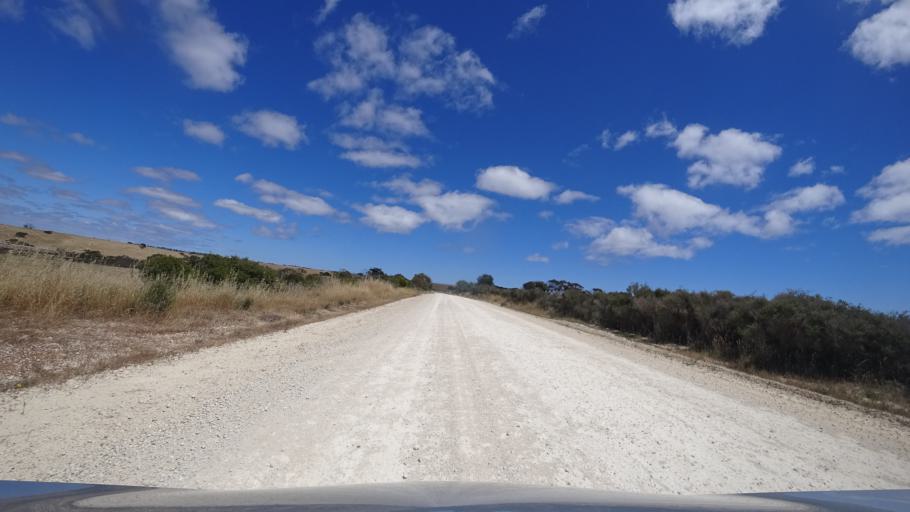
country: AU
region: South Australia
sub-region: Kangaroo Island
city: Kingscote
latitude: -35.6457
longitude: 137.3590
